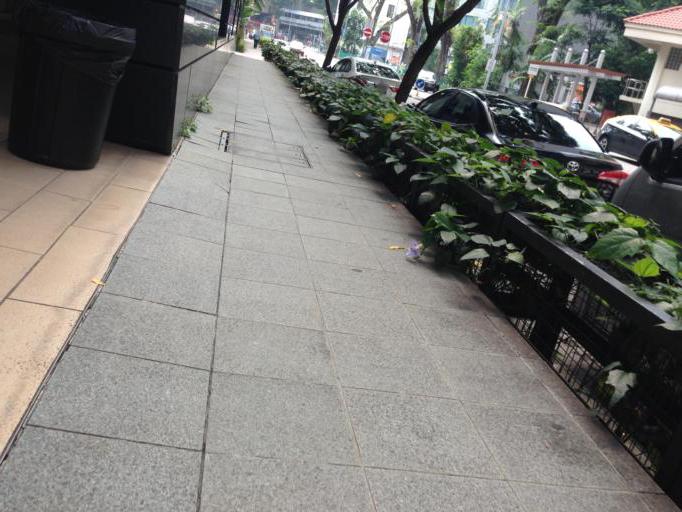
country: SG
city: Singapore
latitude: 1.3033
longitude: 103.8510
